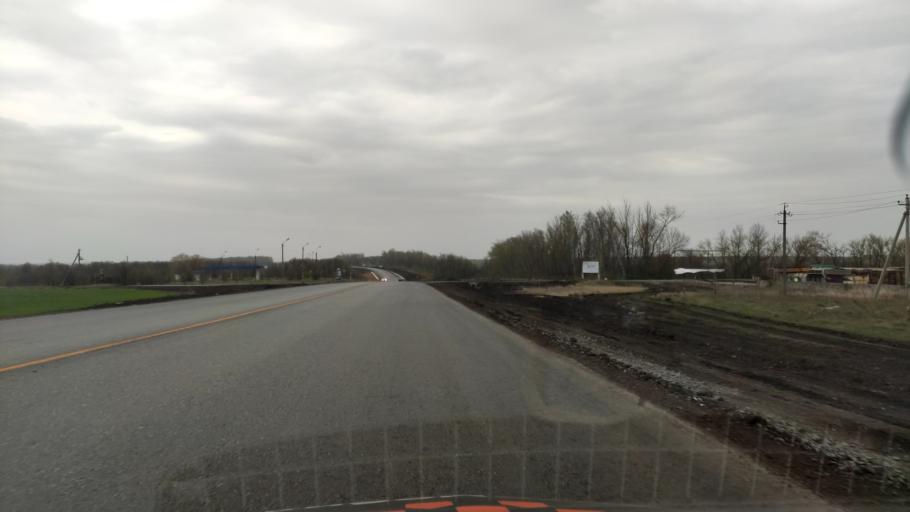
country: RU
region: Kursk
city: Gorshechnoye
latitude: 51.5508
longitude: 38.0428
